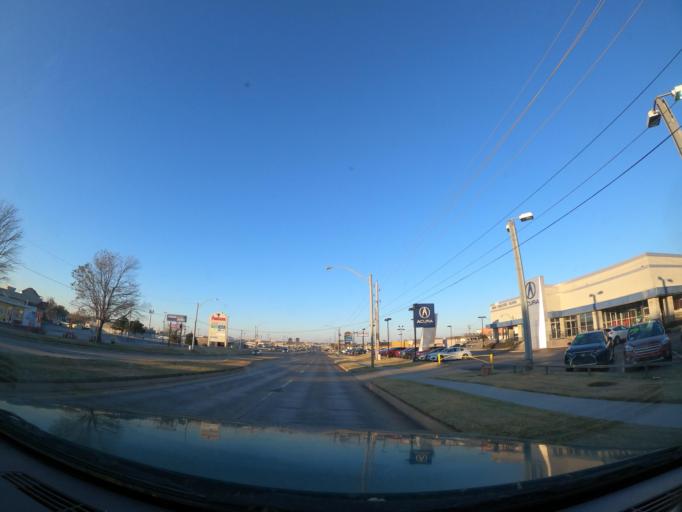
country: US
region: Oklahoma
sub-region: Tulsa County
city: Broken Arrow
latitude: 36.0920
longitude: -95.8864
